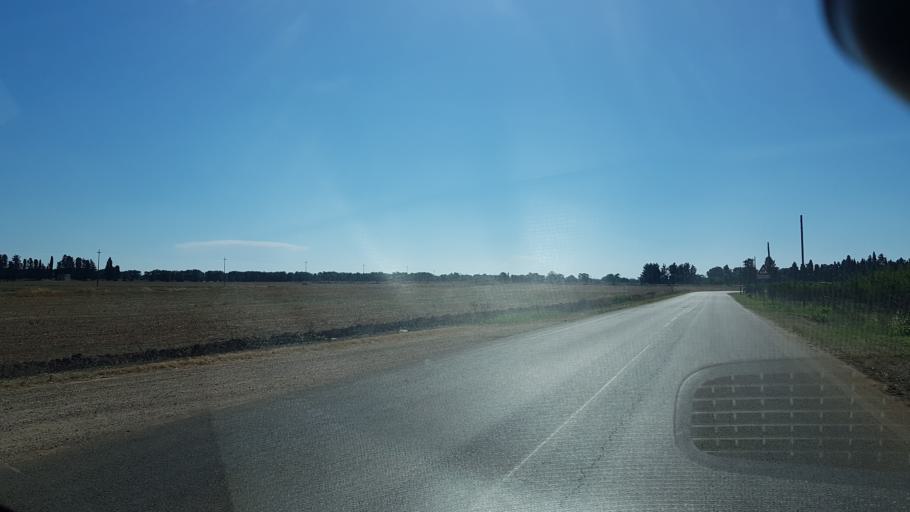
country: IT
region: Apulia
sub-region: Provincia di Brindisi
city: Mesagne
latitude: 40.5568
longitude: 17.8517
